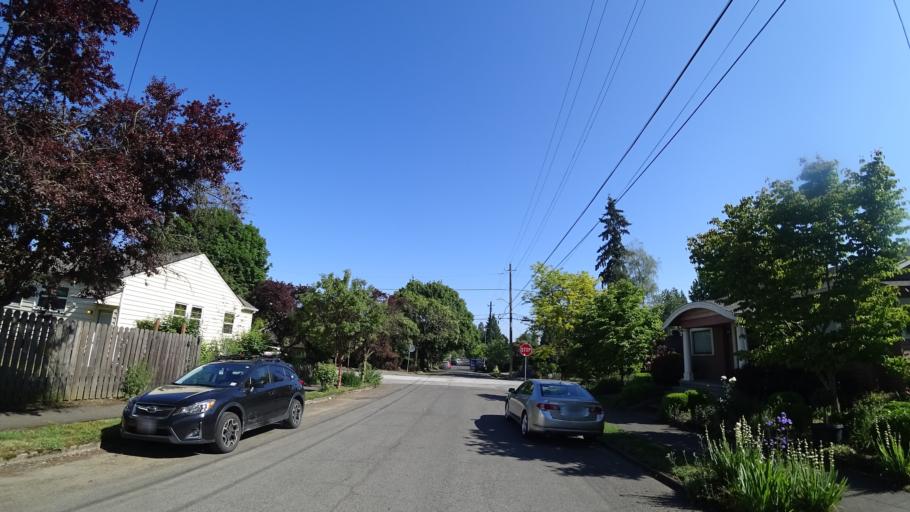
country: US
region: Oregon
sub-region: Multnomah County
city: Portland
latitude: 45.5748
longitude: -122.6633
